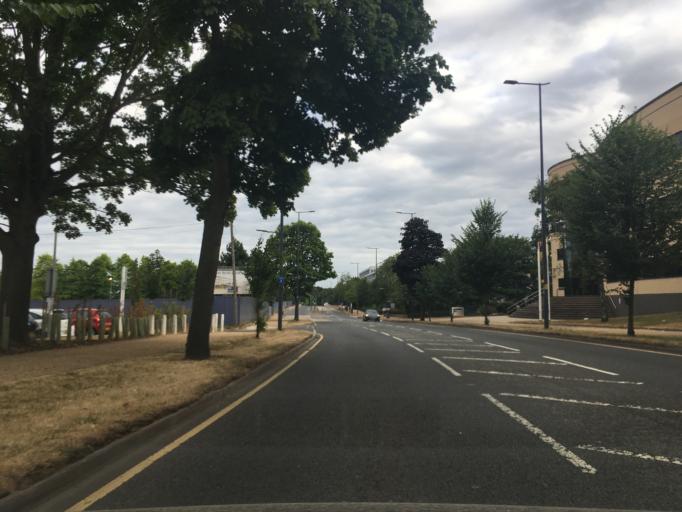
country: GB
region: England
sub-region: Hertfordshire
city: Hemel Hempstead
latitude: 51.7586
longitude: -0.4388
